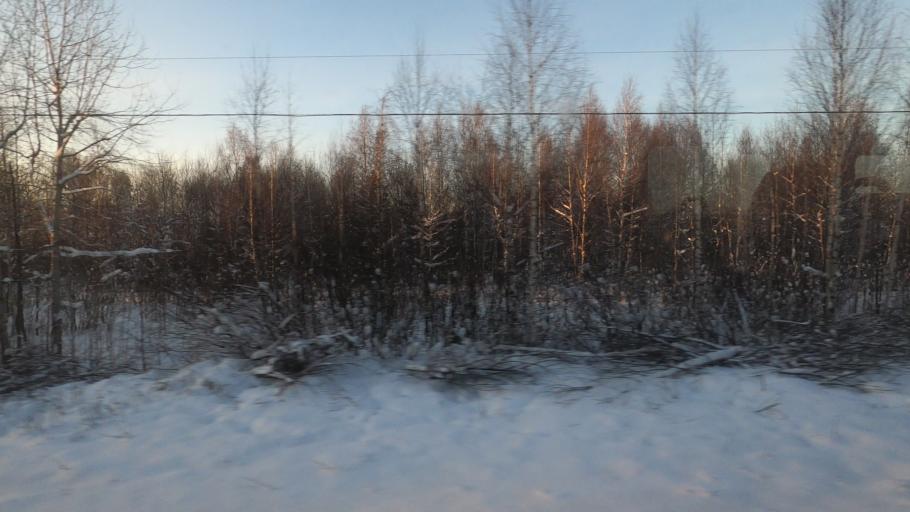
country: RU
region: Moskovskaya
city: Orud'yevo
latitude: 56.4390
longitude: 37.5098
